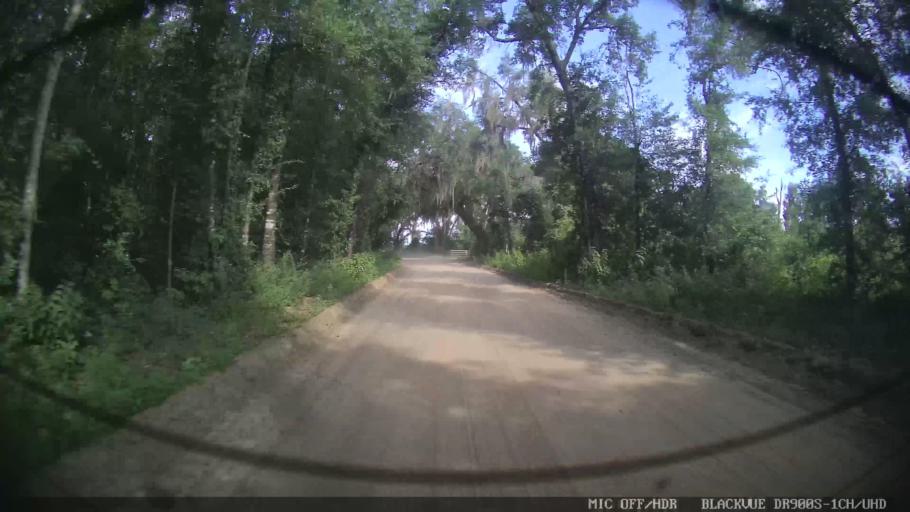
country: US
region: Georgia
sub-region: Lowndes County
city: Valdosta
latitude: 30.6200
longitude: -83.2405
